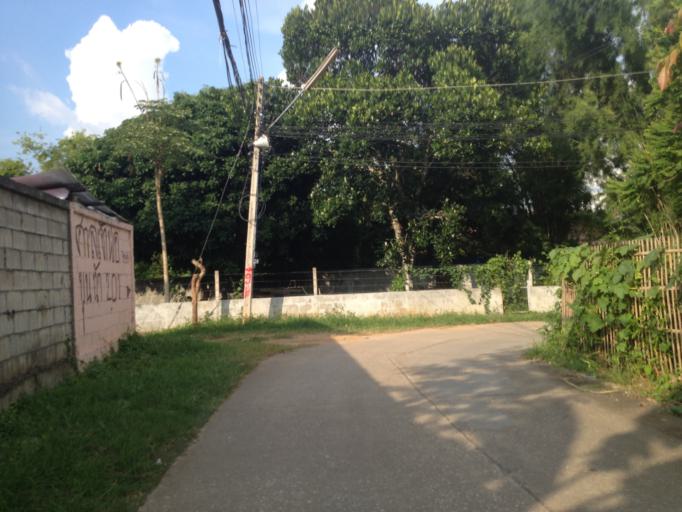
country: TH
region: Chiang Mai
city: Hang Dong
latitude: 18.7245
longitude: 98.9178
